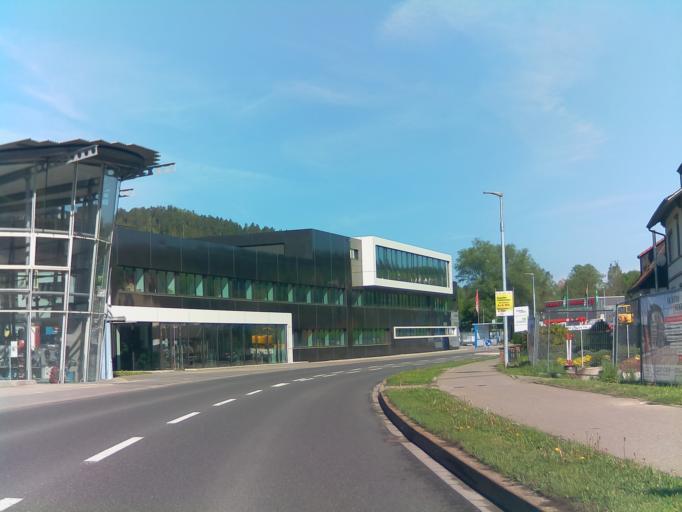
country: DE
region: Baden-Wuerttemberg
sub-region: Karlsruhe Region
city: Rohrdorf
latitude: 48.5706
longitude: 8.6917
